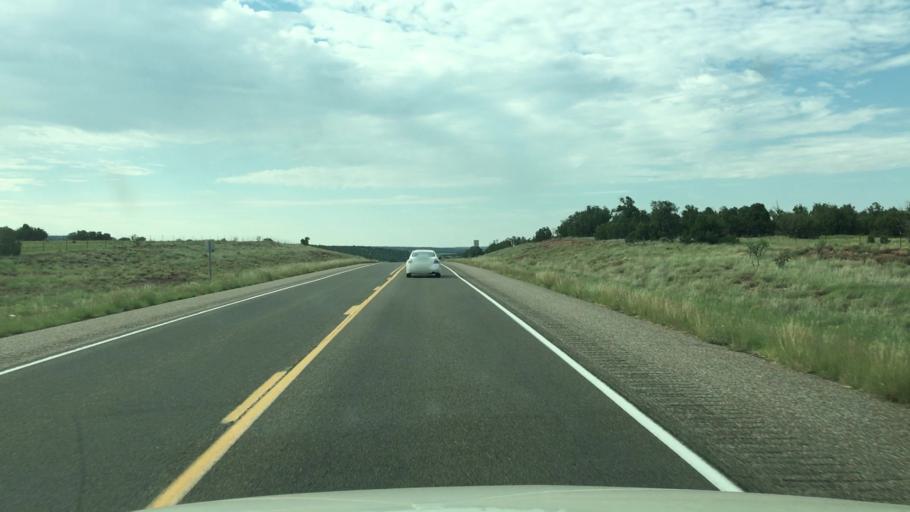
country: US
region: New Mexico
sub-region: Santa Fe County
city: Eldorado at Santa Fe
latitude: 35.3130
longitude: -105.8301
